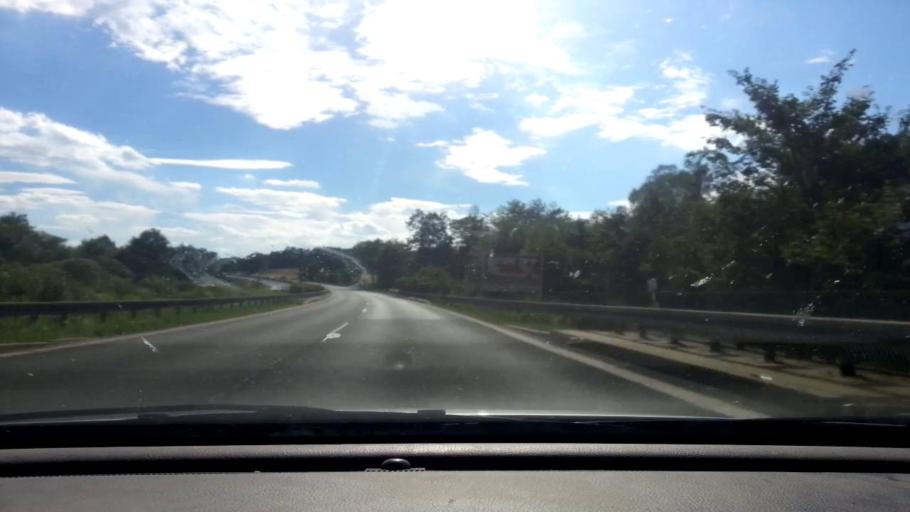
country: DE
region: Bavaria
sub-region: Upper Franconia
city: Neudrossenfeld
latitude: 50.0305
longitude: 11.4617
